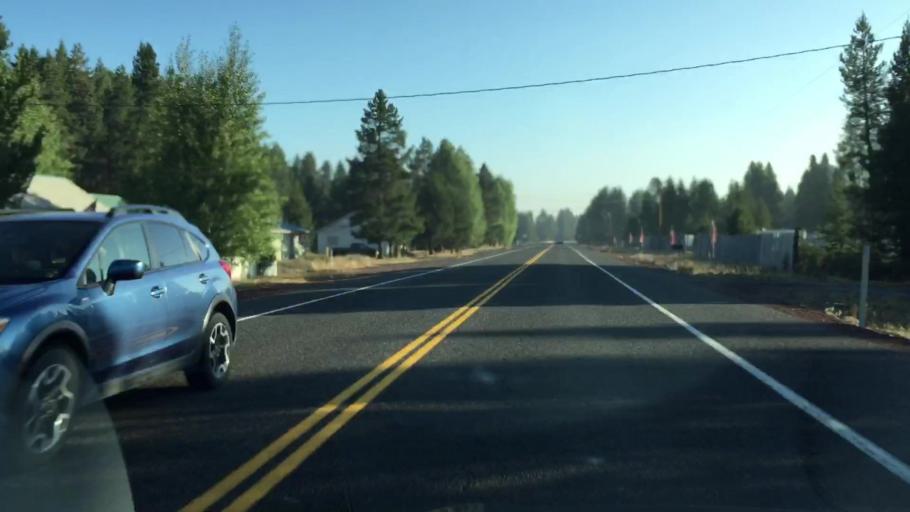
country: US
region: Oregon
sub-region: Deschutes County
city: La Pine
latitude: 43.4556
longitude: -121.7014
